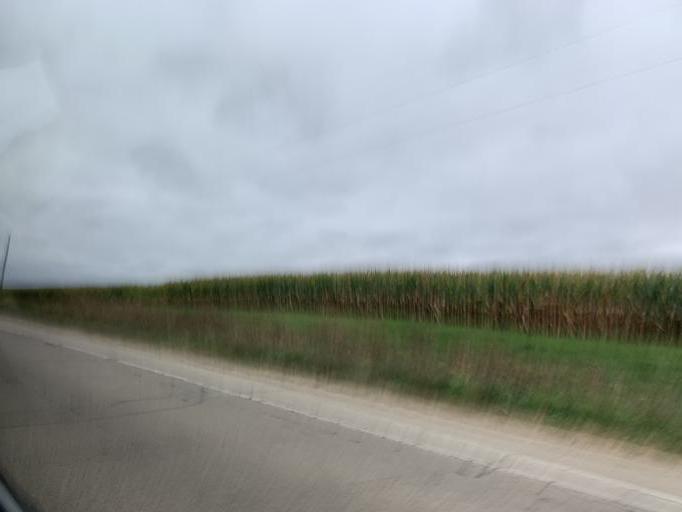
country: US
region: Wisconsin
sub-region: Grant County
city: Muscoda
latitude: 43.2198
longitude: -90.4903
